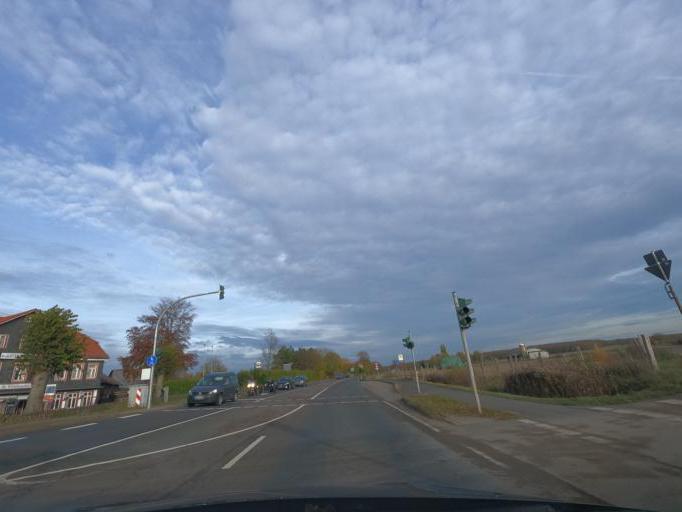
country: DE
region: Lower Saxony
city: Cremlingen
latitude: 52.2991
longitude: 10.6010
